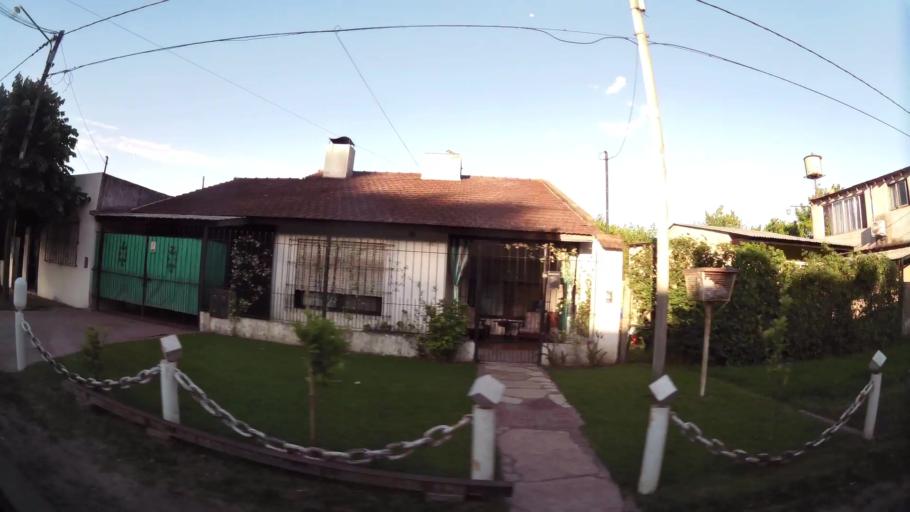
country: AR
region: Buenos Aires
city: Santa Catalina - Dique Lujan
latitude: -34.4654
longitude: -58.7524
